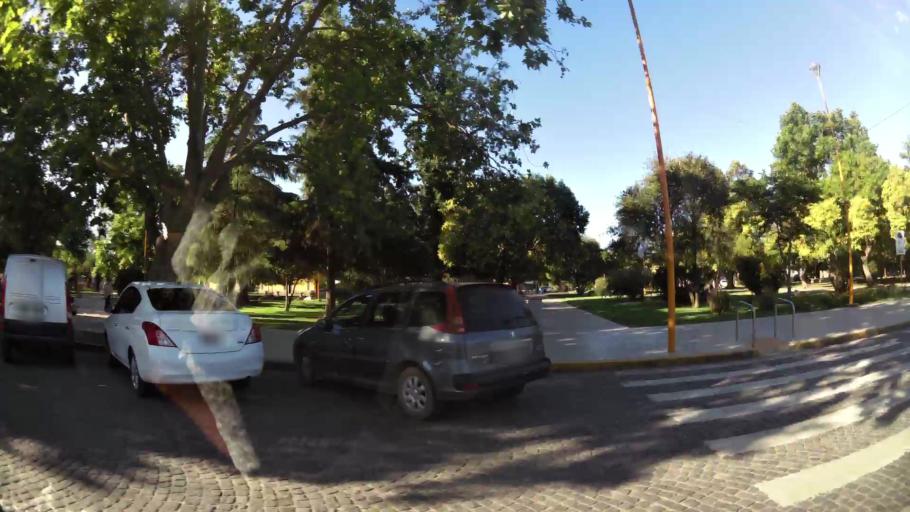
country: AR
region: Cordoba
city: San Francisco
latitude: -31.4354
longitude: -62.0865
